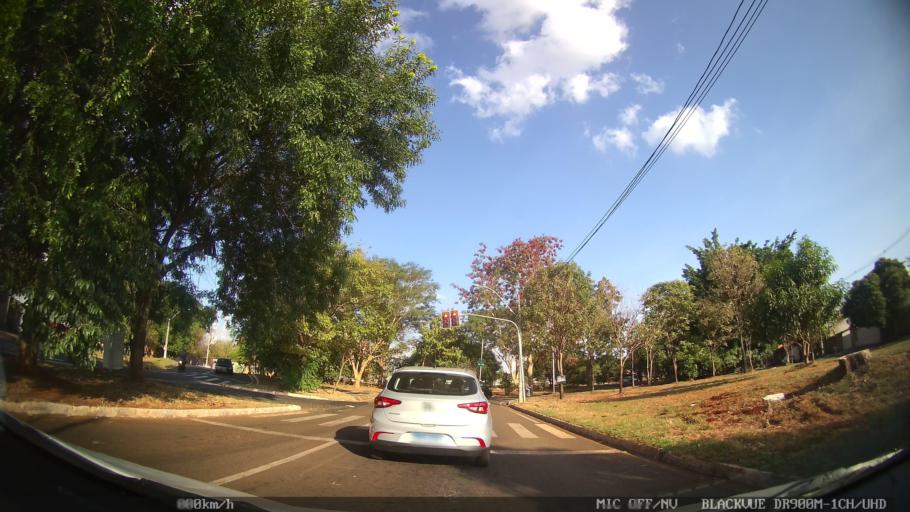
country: BR
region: Sao Paulo
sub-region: Ribeirao Preto
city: Ribeirao Preto
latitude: -21.1545
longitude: -47.8414
